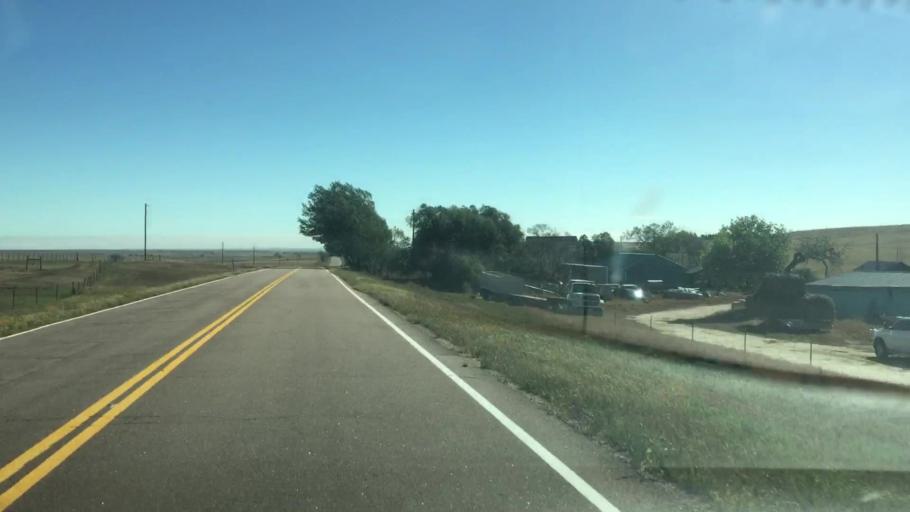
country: US
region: Colorado
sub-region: Lincoln County
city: Limon
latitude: 39.2882
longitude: -103.9609
